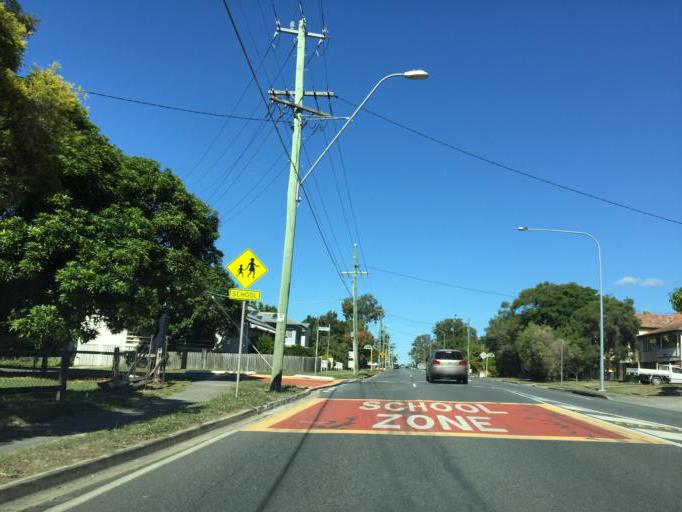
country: AU
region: Queensland
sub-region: Brisbane
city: Everton Park
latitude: -27.4132
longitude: 152.9926
